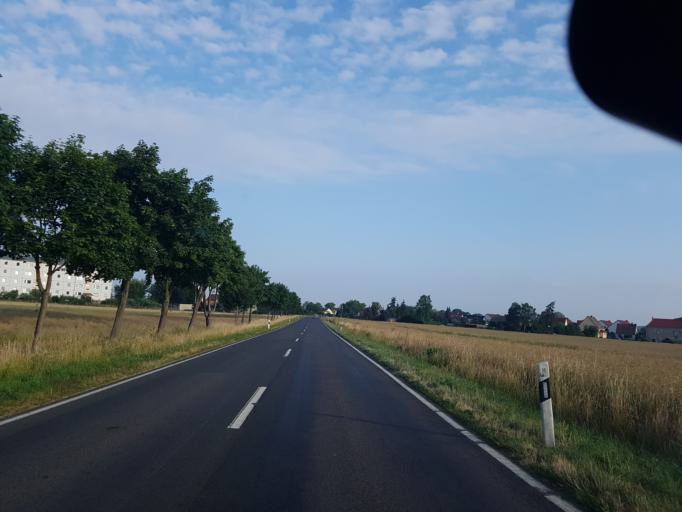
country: DE
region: Brandenburg
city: Schlieben
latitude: 51.7191
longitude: 13.3824
